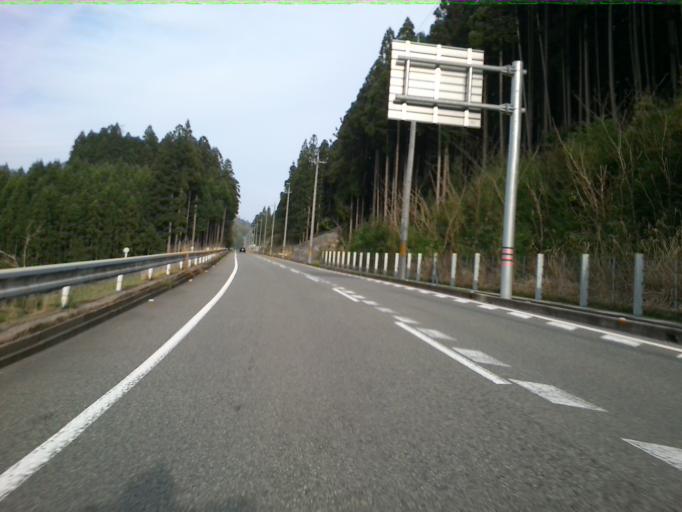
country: JP
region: Hyogo
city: Sasayama
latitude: 35.0658
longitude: 135.4044
